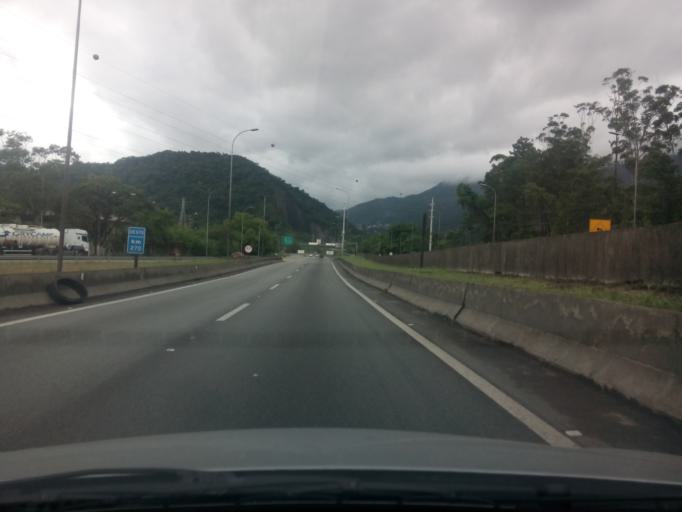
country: BR
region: Sao Paulo
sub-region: Cubatao
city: Cubatao
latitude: -23.8870
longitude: -46.4347
